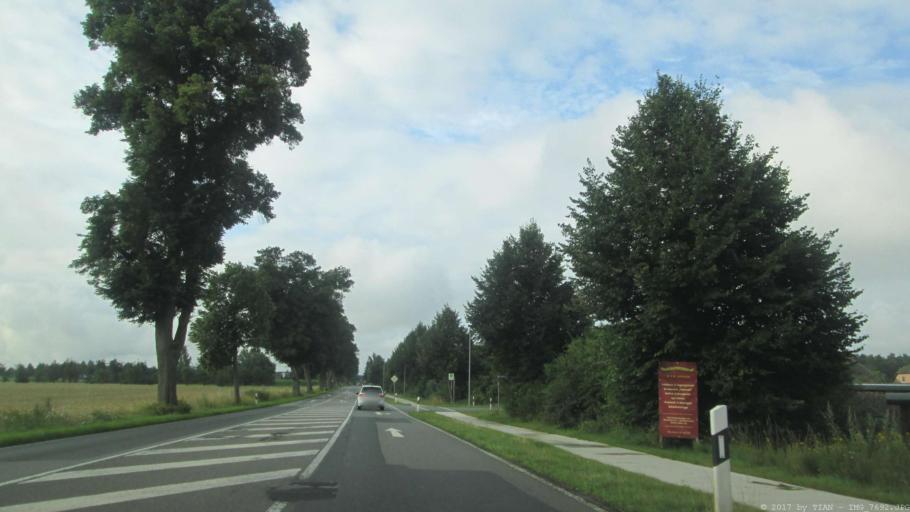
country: DE
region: Lower Saxony
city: Bodenteich
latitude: 52.8476
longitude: 10.6820
